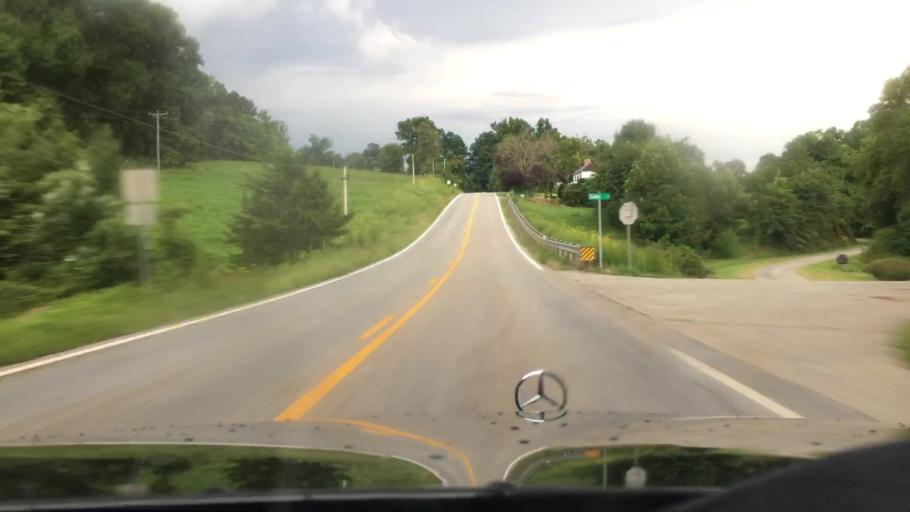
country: US
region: Virginia
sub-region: Nelson County
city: Lovingston
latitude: 37.7788
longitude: -78.9802
